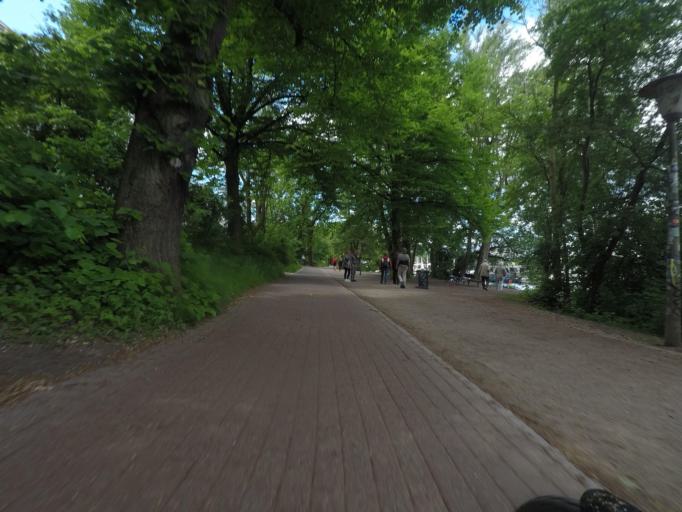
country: DE
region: Hamburg
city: St. Georg
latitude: 53.5589
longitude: 10.0070
